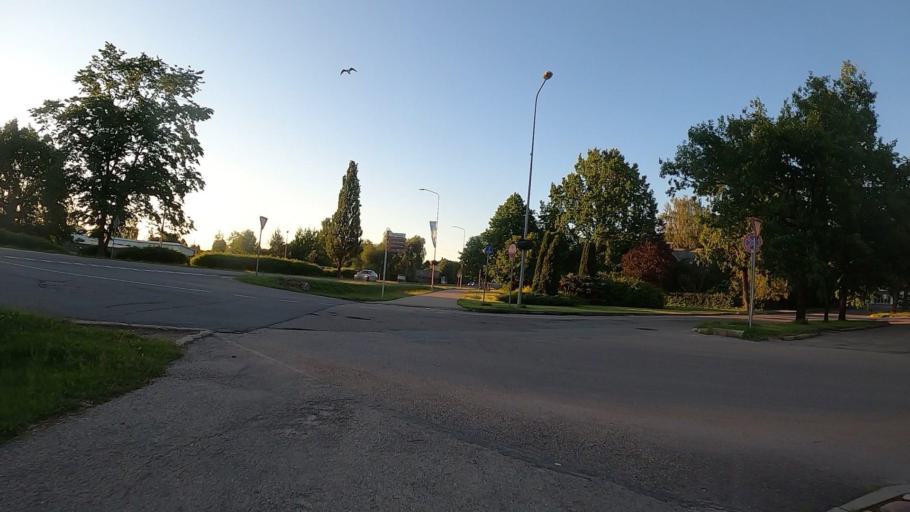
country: LV
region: Salaspils
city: Salaspils
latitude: 56.8585
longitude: 24.3478
